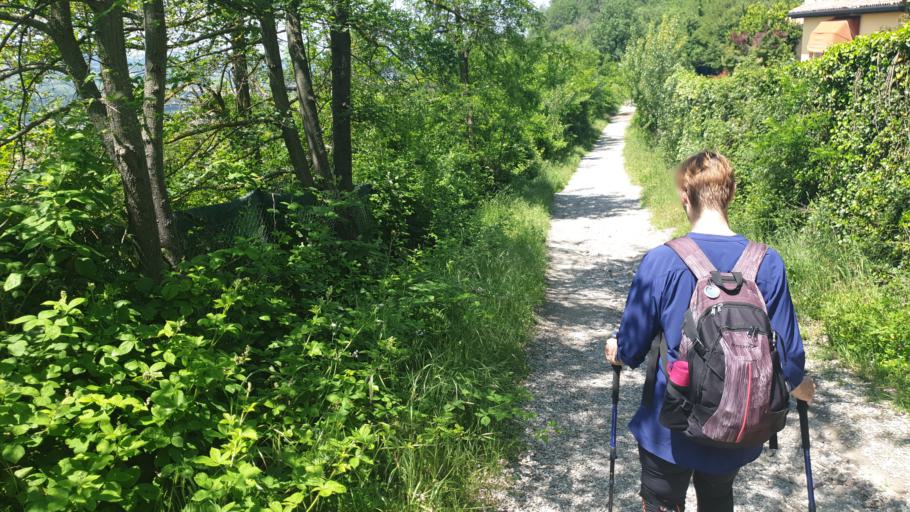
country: IT
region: Emilia-Romagna
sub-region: Provincia di Bologna
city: Casalecchio di Reno
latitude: 44.4751
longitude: 11.2925
